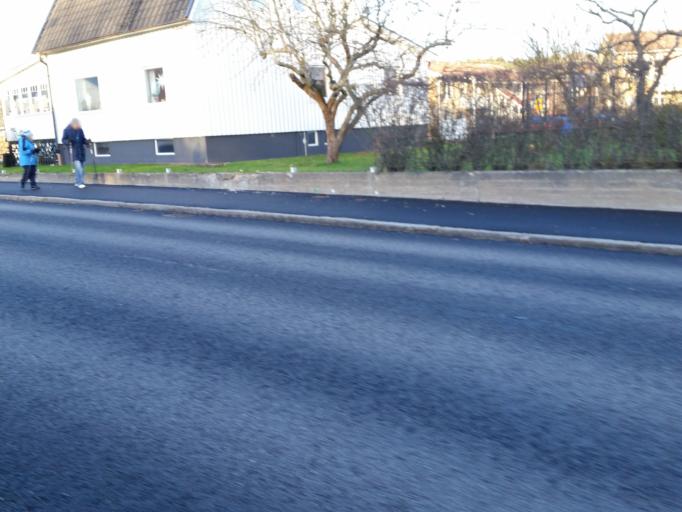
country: SE
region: Vaestra Goetaland
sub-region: Trollhattan
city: Trollhattan
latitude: 58.2831
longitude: 12.2618
